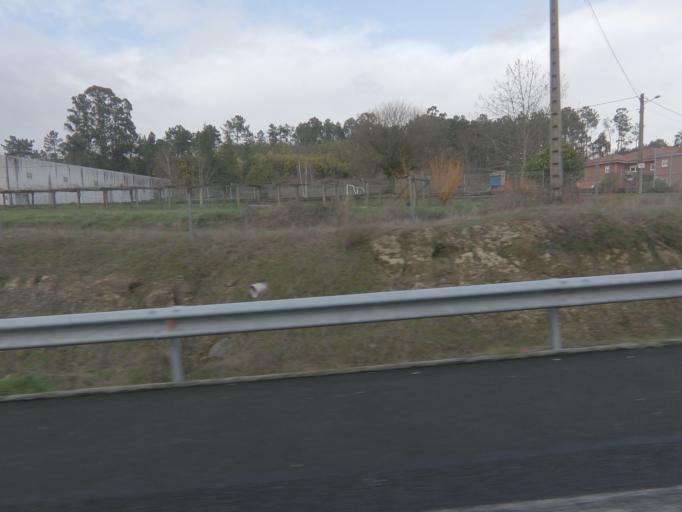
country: ES
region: Galicia
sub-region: Provincia da Coruna
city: Ribeira
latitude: 42.7477
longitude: -8.3861
